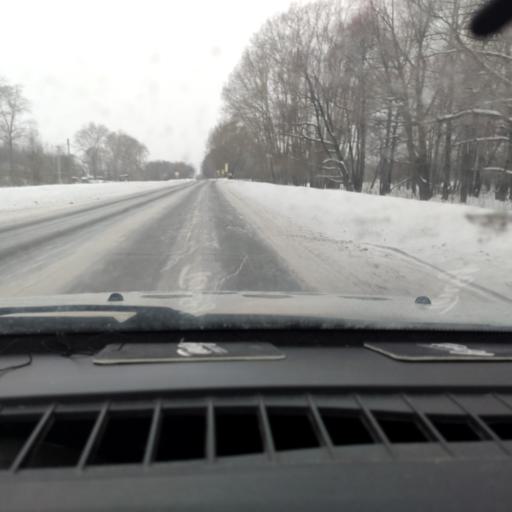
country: RU
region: Perm
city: Kondratovo
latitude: 57.9366
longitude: 56.0572
